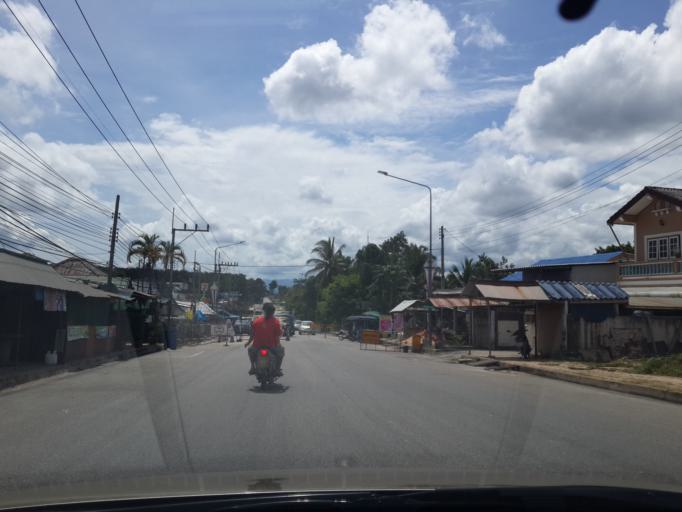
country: TH
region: Narathiwat
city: Rueso
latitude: 6.3832
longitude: 101.5115
